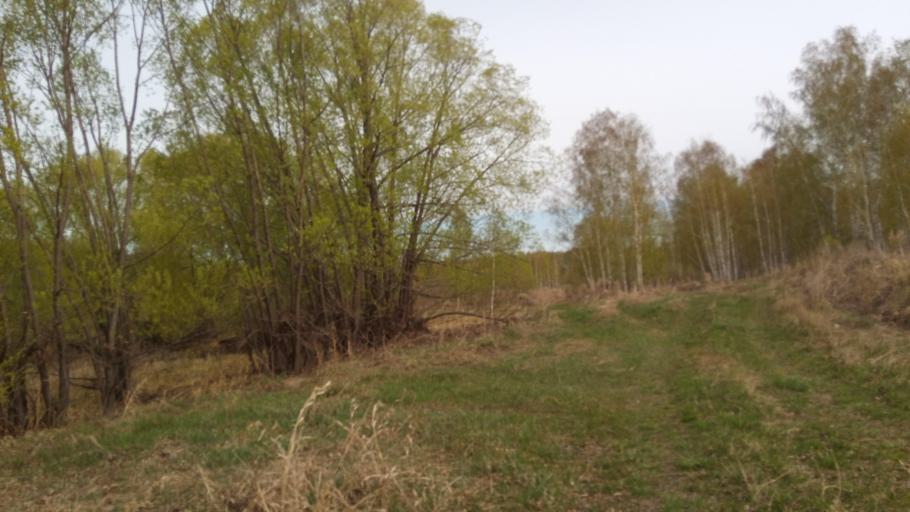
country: RU
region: Chelyabinsk
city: Timiryazevskiy
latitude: 55.0007
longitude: 60.8519
